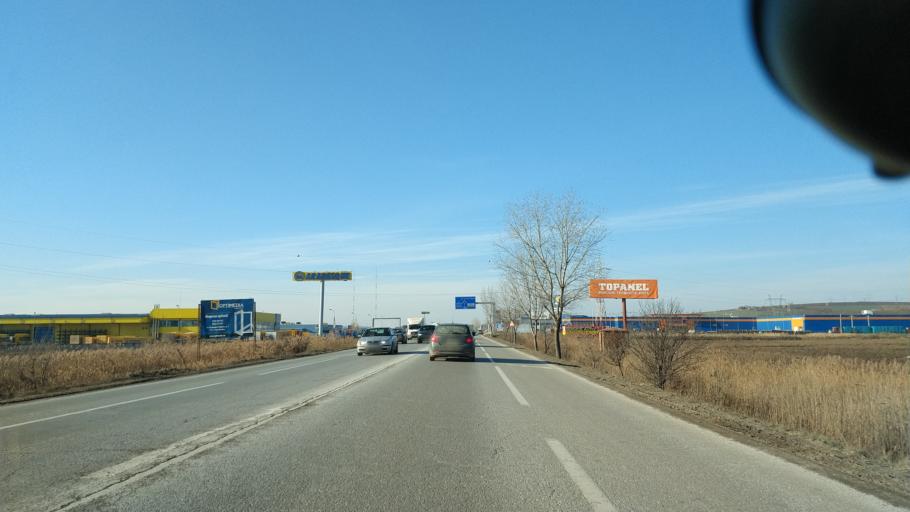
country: RO
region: Iasi
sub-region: Comuna Valea Lupului
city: Valea Lupului
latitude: 47.1797
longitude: 27.4787
